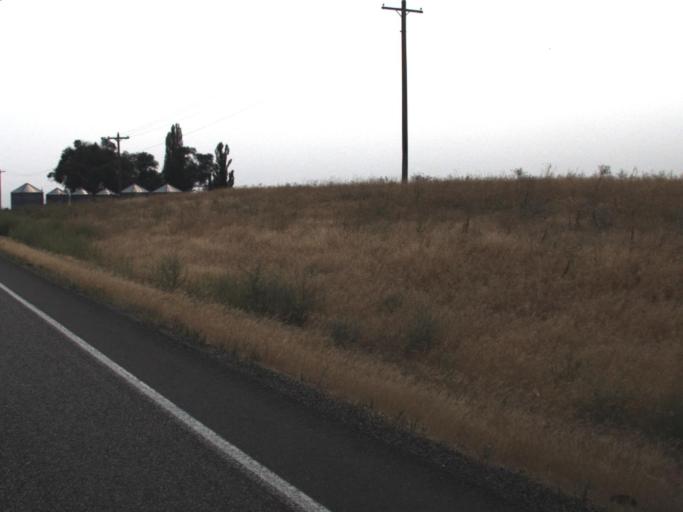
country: US
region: Oregon
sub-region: Morrow County
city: Irrigon
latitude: 46.0736
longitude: -119.6021
